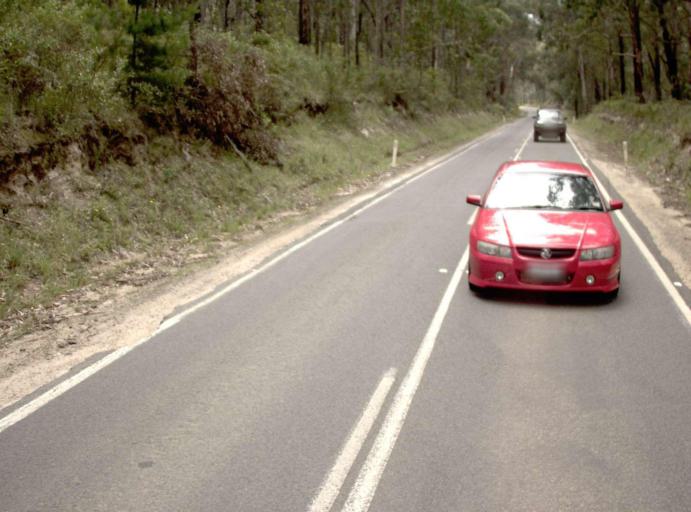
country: AU
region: Victoria
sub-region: Latrobe
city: Traralgon
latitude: -38.4236
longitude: 146.7449
